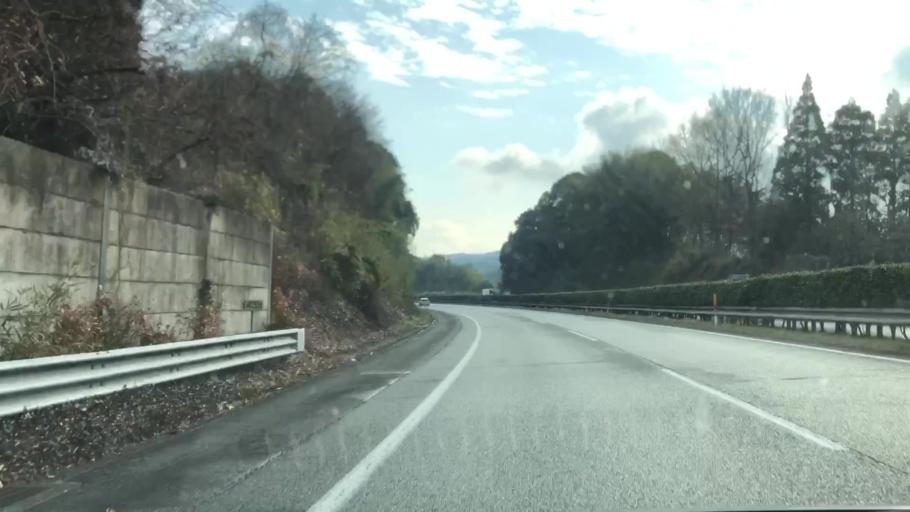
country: JP
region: Kumamoto
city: Tamana
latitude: 33.0068
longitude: 130.5828
